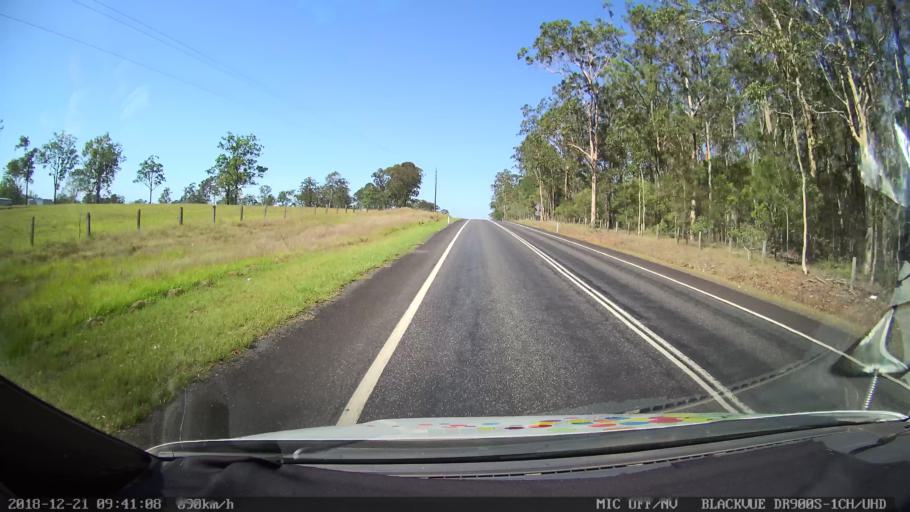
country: AU
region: New South Wales
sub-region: Clarence Valley
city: Grafton
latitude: -29.5818
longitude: 152.9601
